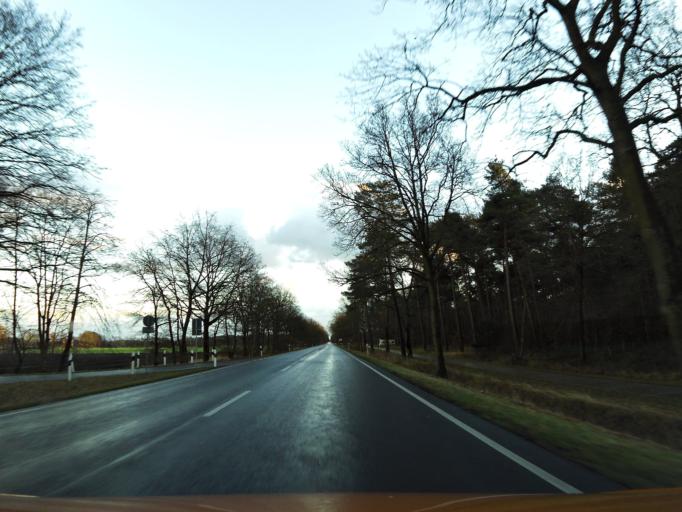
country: DE
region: Lower Saxony
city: Uetze
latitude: 52.4724
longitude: 10.2760
